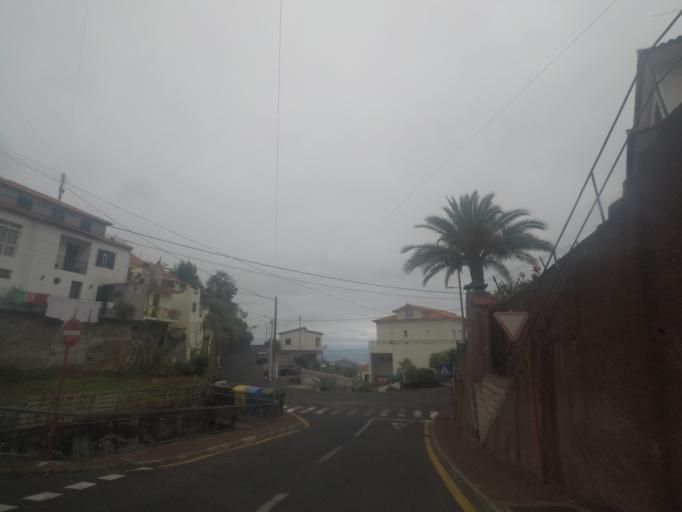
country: PT
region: Madeira
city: Camara de Lobos
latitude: 32.6745
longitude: -16.9786
